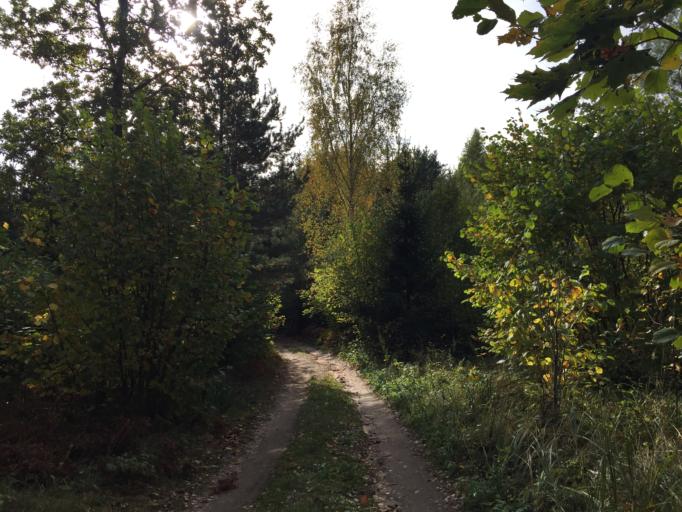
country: LV
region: Jaunpils
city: Jaunpils
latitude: 56.5962
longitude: 23.0142
